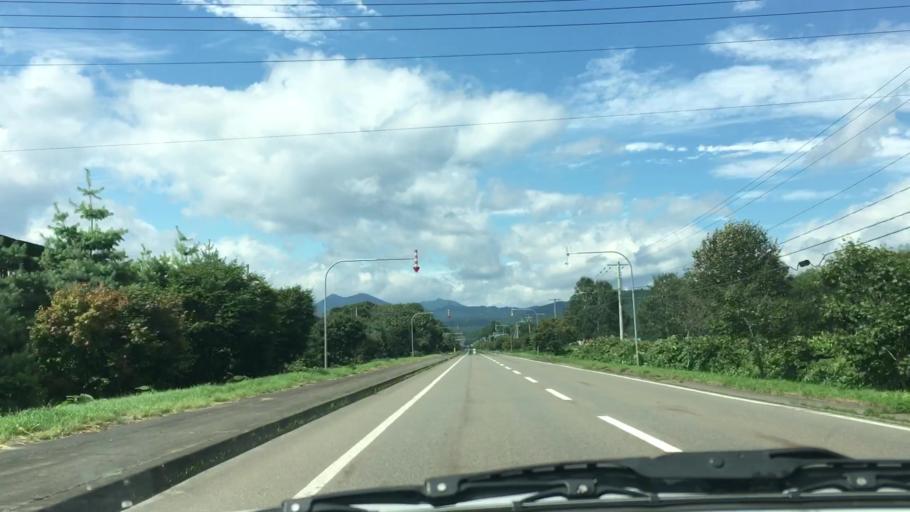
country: JP
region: Hokkaido
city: Otofuke
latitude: 43.3117
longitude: 143.3076
